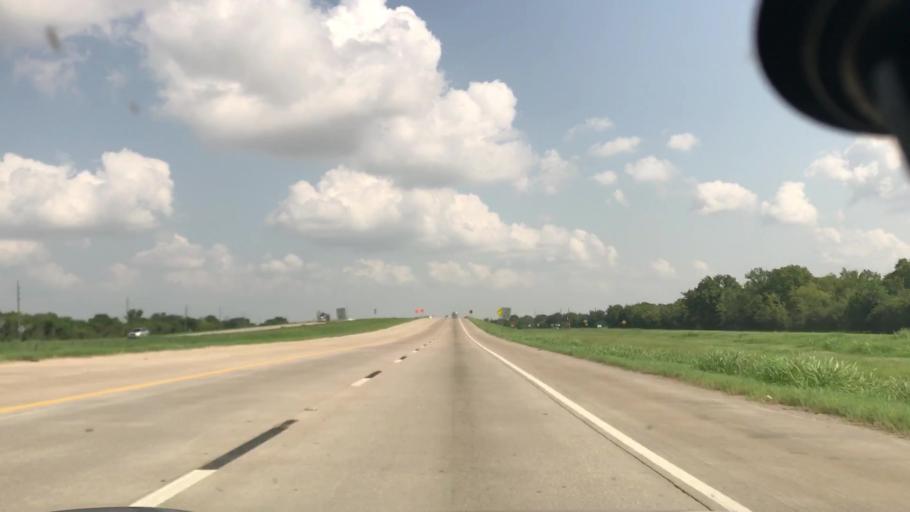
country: US
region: Texas
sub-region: Brazoria County
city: Iowa Colony
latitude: 29.5076
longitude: -95.3877
